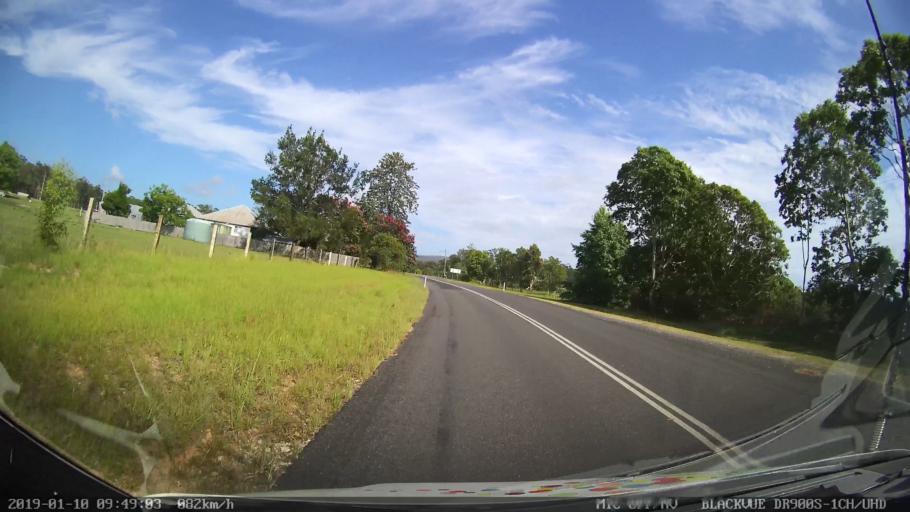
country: AU
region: New South Wales
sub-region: Coffs Harbour
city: Nana Glen
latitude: -30.0657
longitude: 152.9829
